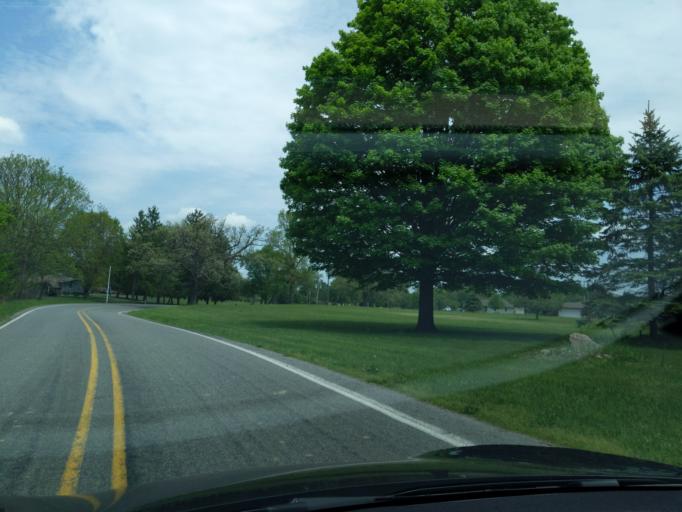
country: US
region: Michigan
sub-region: Ingham County
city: Stockbridge
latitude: 42.4618
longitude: -84.1647
